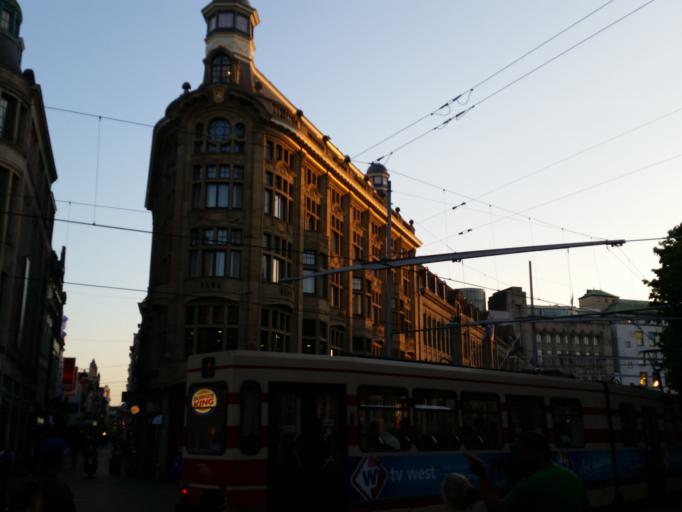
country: NL
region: South Holland
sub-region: Gemeente Den Haag
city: The Hague
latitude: 52.0783
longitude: 4.3138
